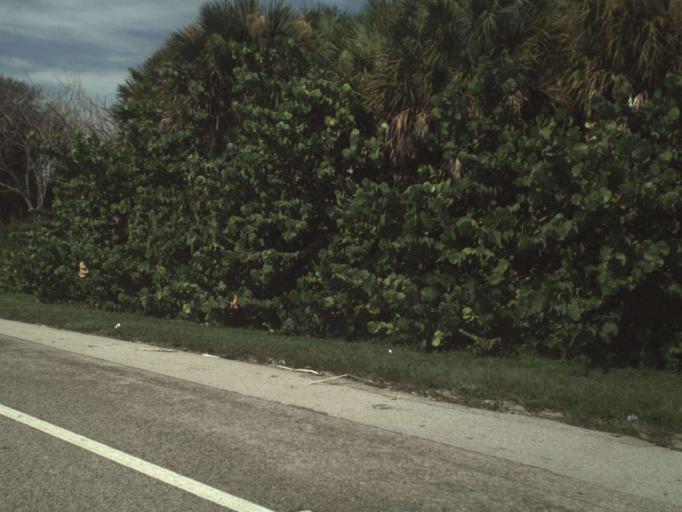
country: US
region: Florida
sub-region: Palm Beach County
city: Mangonia Park
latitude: 26.7482
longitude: -80.0905
